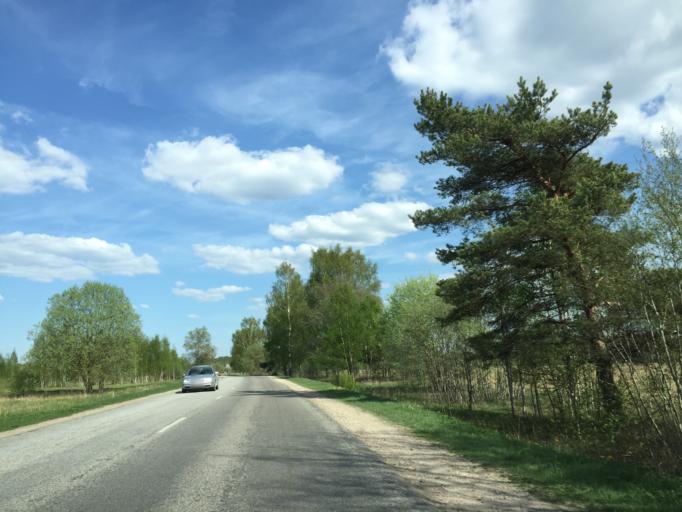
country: LV
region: Limbazu Rajons
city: Limbazi
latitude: 57.5115
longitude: 24.7413
